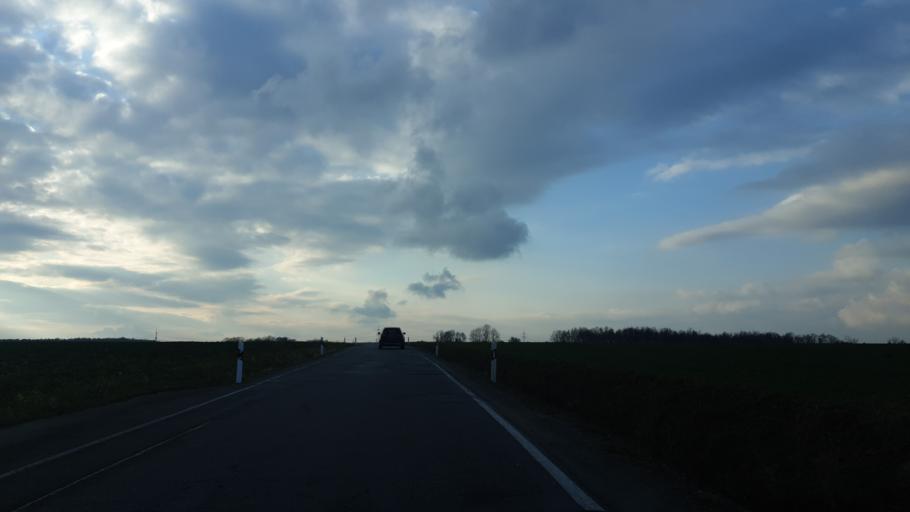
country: DE
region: Saxony
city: Niederdorf
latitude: 50.7544
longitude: 12.8144
